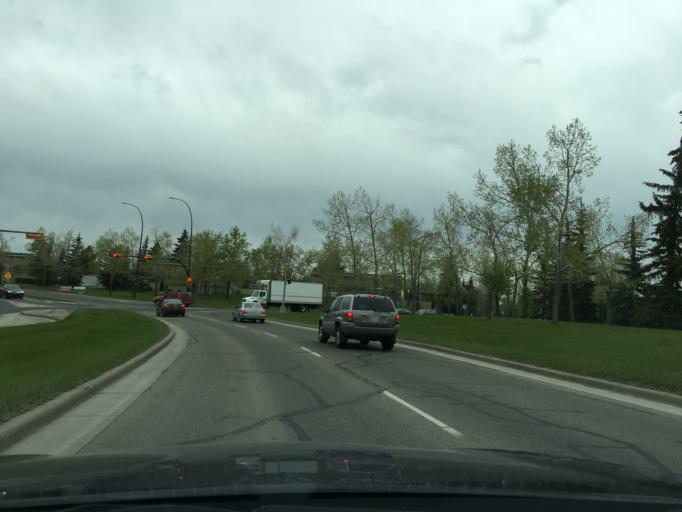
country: CA
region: Alberta
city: Calgary
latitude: 50.9530
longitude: -114.0604
